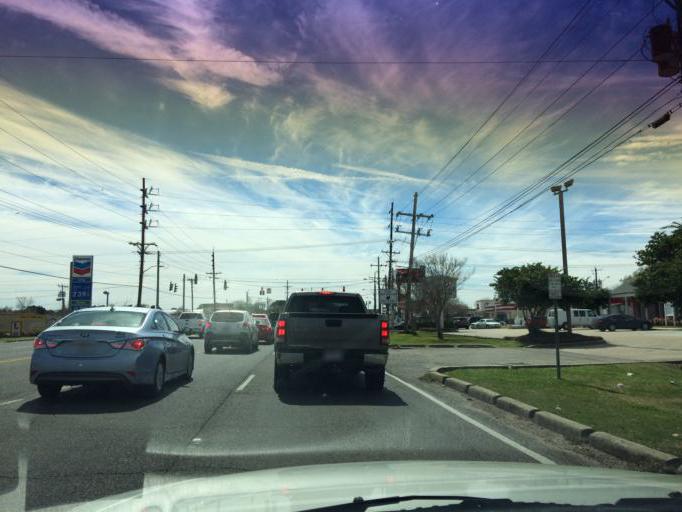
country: US
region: Louisiana
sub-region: Lafayette Parish
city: Lafayette
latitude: 30.1951
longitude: -92.0577
